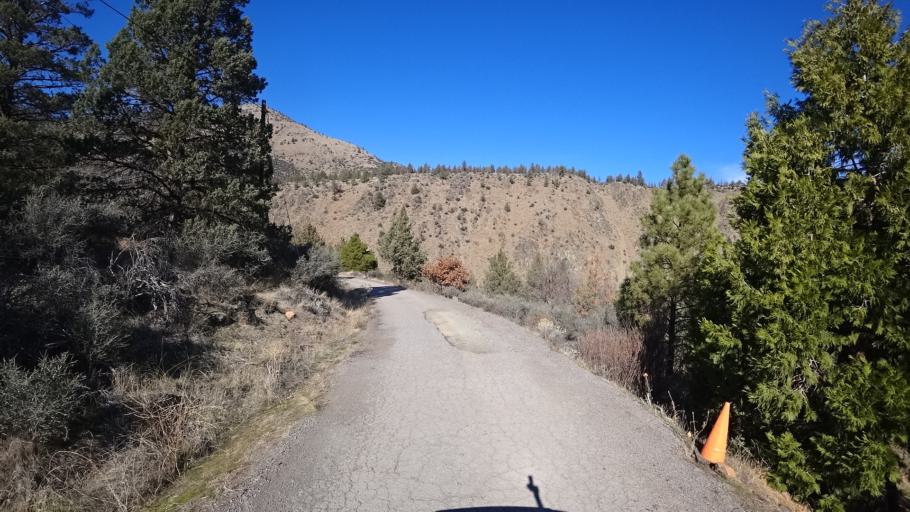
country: US
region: California
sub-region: Siskiyou County
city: Yreka
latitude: 41.8024
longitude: -122.6012
